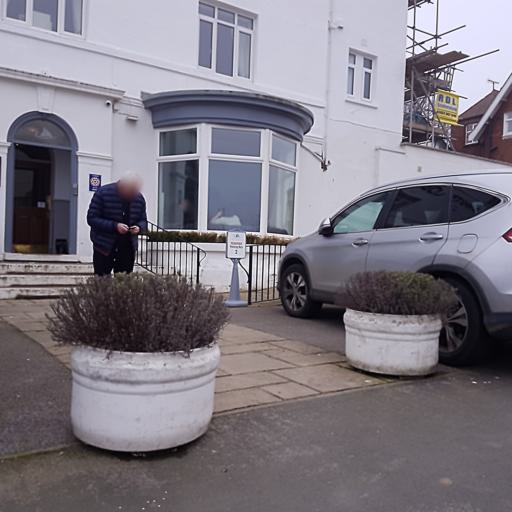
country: GB
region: England
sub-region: North Yorkshire
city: Filey
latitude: 54.2046
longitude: -0.2866
